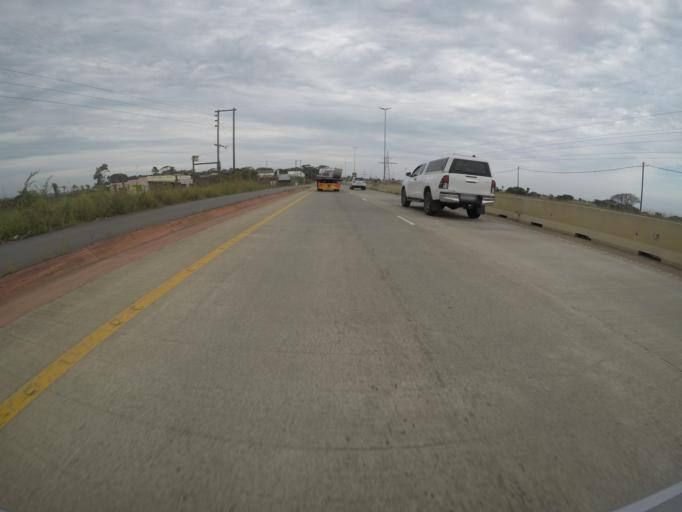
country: ZA
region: Eastern Cape
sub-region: Buffalo City Metropolitan Municipality
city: East London
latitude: -32.9366
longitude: 27.9849
